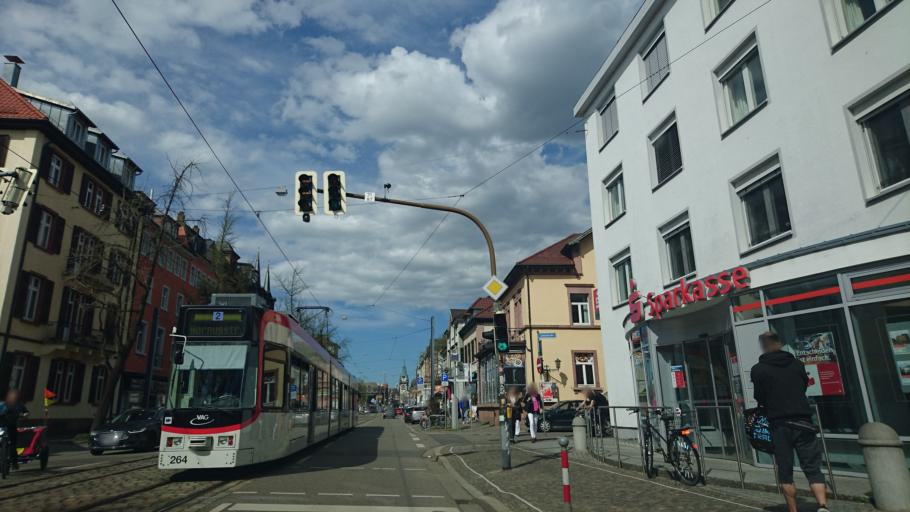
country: DE
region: Baden-Wuerttemberg
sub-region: Freiburg Region
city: Freiburg
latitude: 47.9868
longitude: 7.8476
